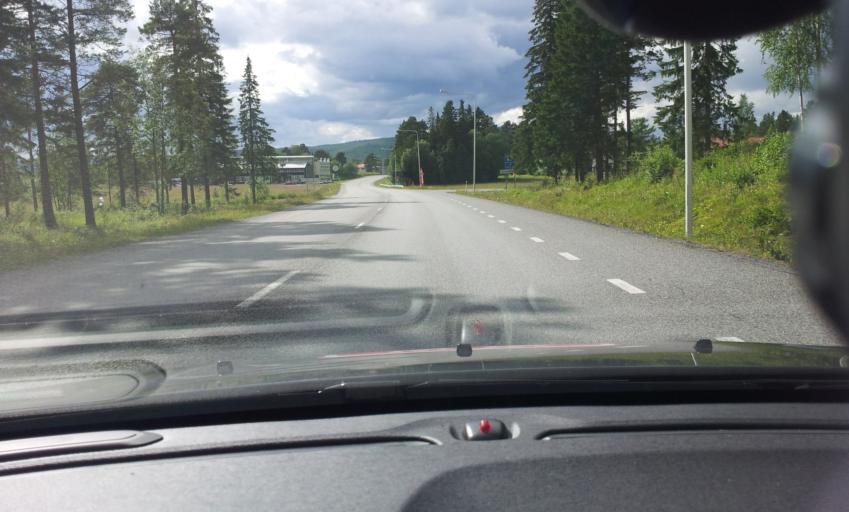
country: SE
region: Jaemtland
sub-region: Are Kommun
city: Jarpen
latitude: 63.3411
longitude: 13.4855
